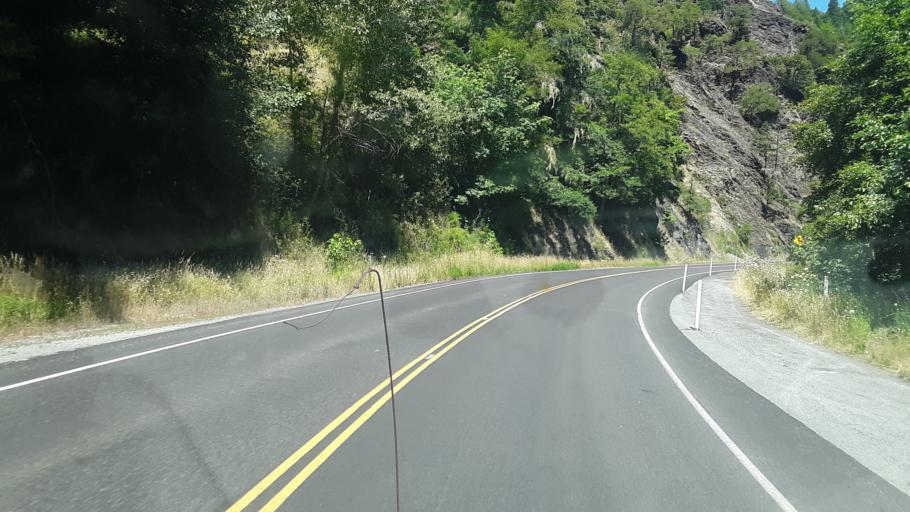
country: US
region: Oregon
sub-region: Josephine County
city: Cave Junction
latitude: 41.8783
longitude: -123.8312
